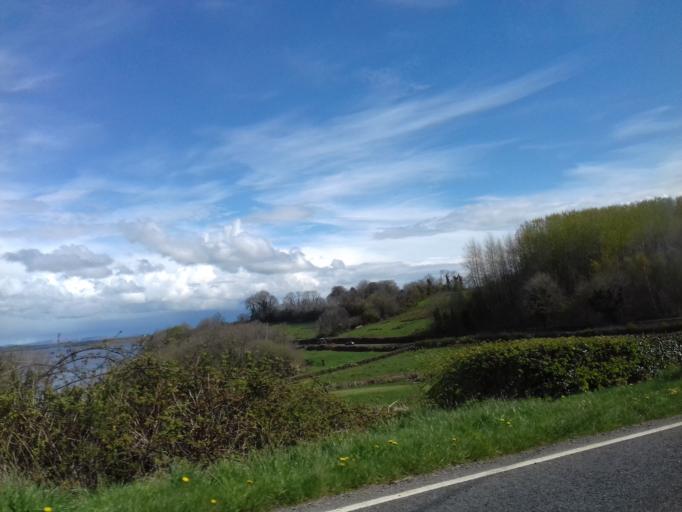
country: GB
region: Northern Ireland
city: Irvinestown
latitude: 54.4514
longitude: -7.8074
